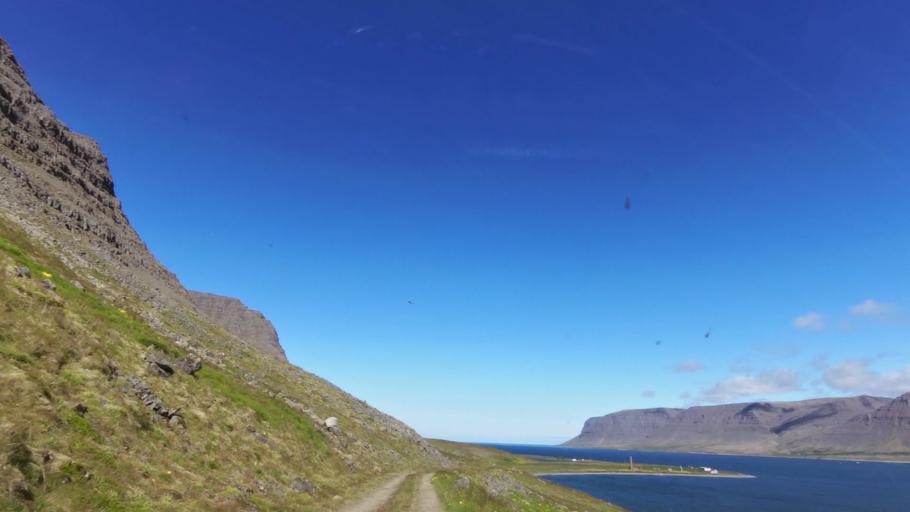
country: IS
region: West
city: Olafsvik
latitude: 65.6339
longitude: -23.9229
